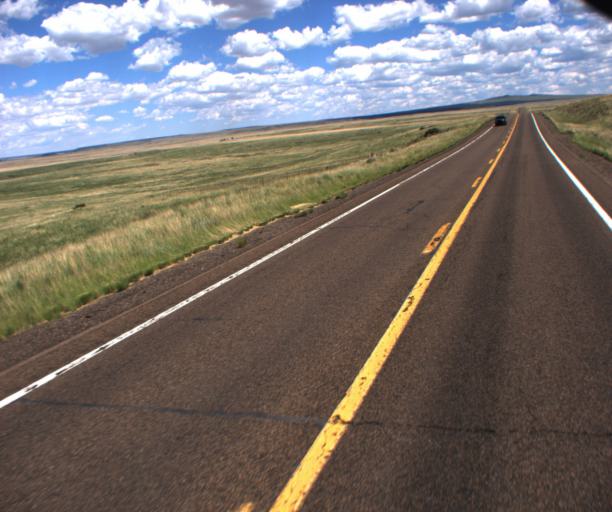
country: US
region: Arizona
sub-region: Apache County
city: Springerville
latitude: 34.1961
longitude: -109.3799
